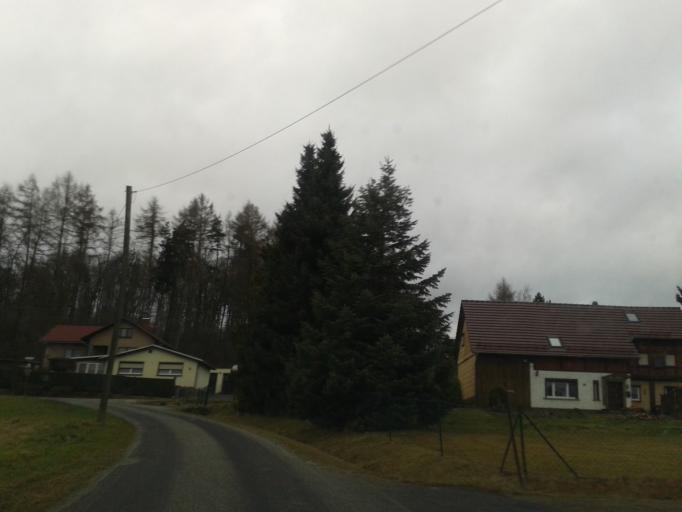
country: DE
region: Saxony
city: Leutersdorf
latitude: 50.9557
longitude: 14.6272
